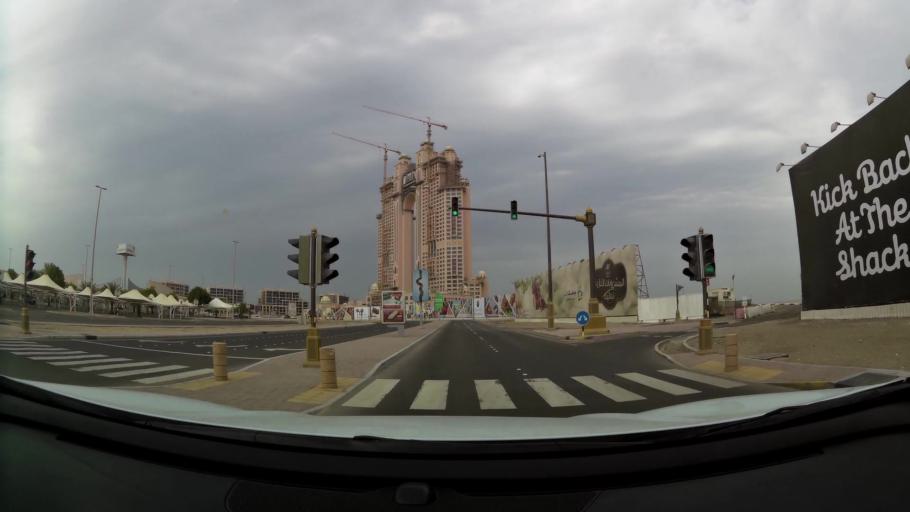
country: AE
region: Abu Dhabi
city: Abu Dhabi
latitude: 24.4780
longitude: 54.3245
